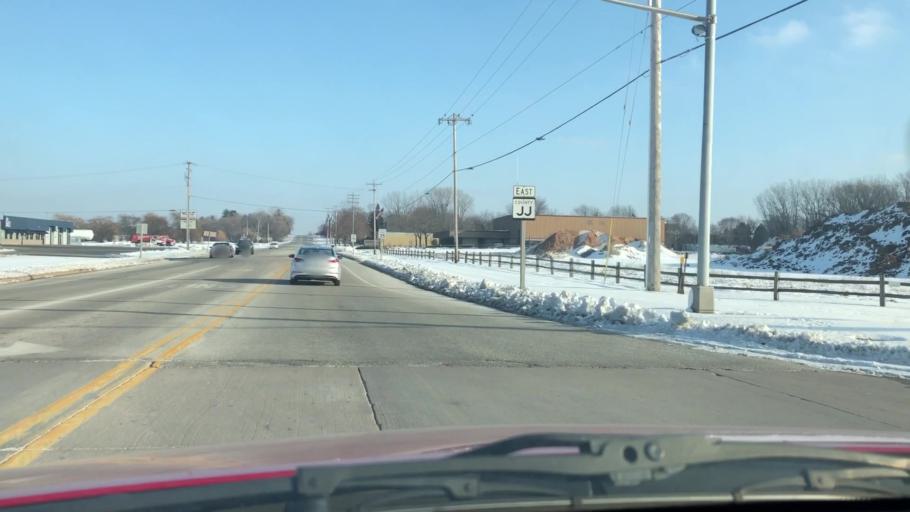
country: US
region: Wisconsin
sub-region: Outagamie County
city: Appleton
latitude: 44.3164
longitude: -88.4147
